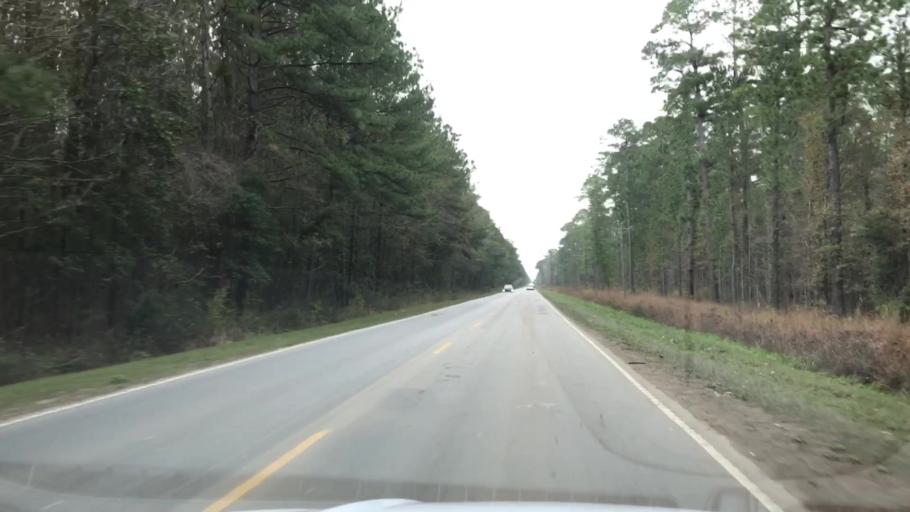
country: US
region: South Carolina
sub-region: Jasper County
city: Ridgeland
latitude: 32.3822
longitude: -80.9101
